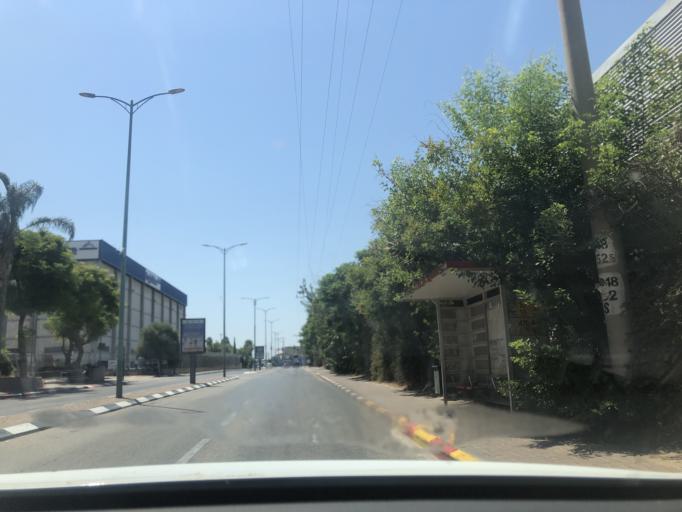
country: IL
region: Central District
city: Lod
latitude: 31.9682
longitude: 34.8982
